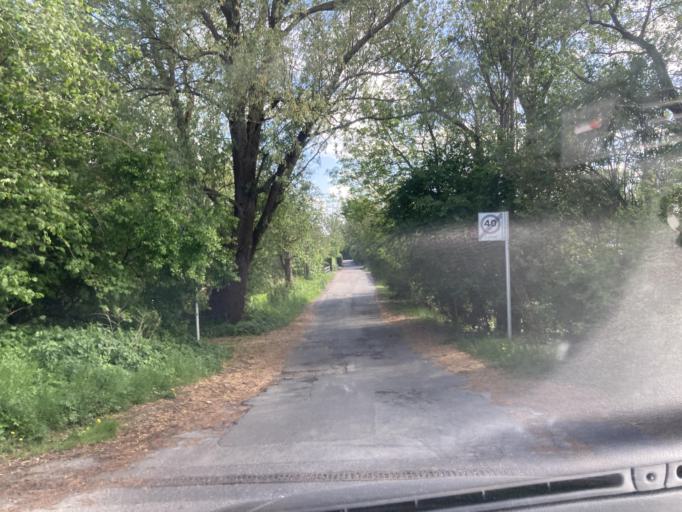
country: DK
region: Capital Region
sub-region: Gribskov Kommune
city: Helsinge
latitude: 56.0049
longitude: 12.1103
